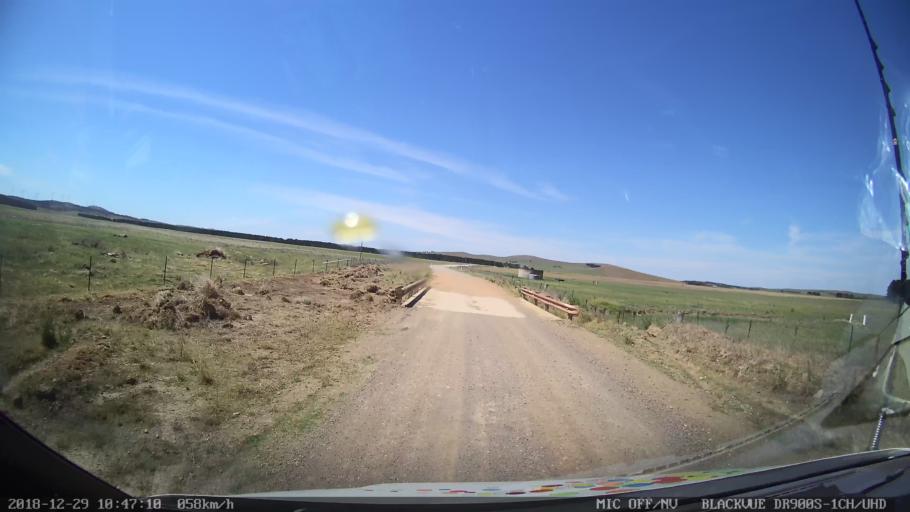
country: AU
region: New South Wales
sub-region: Palerang
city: Bungendore
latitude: -35.0570
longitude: 149.5159
